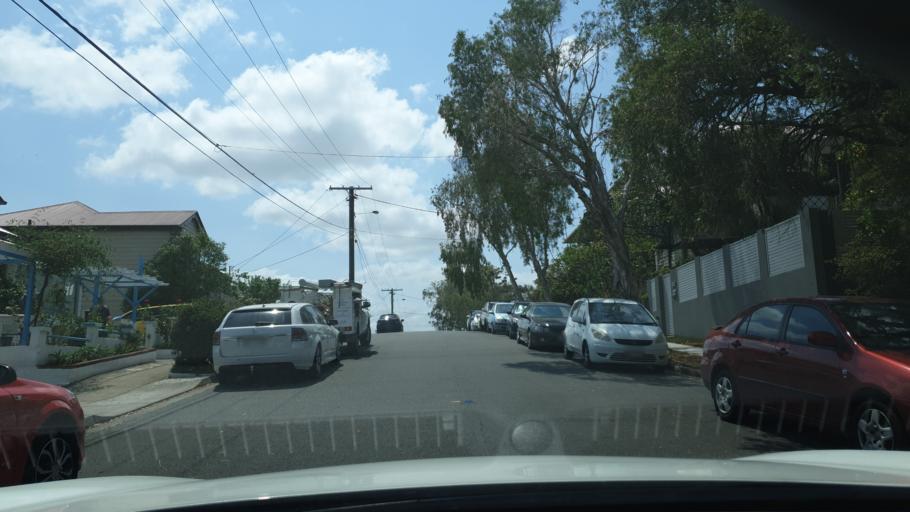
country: AU
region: Queensland
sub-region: Brisbane
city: South Brisbane
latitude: -27.4855
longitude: 153.0168
